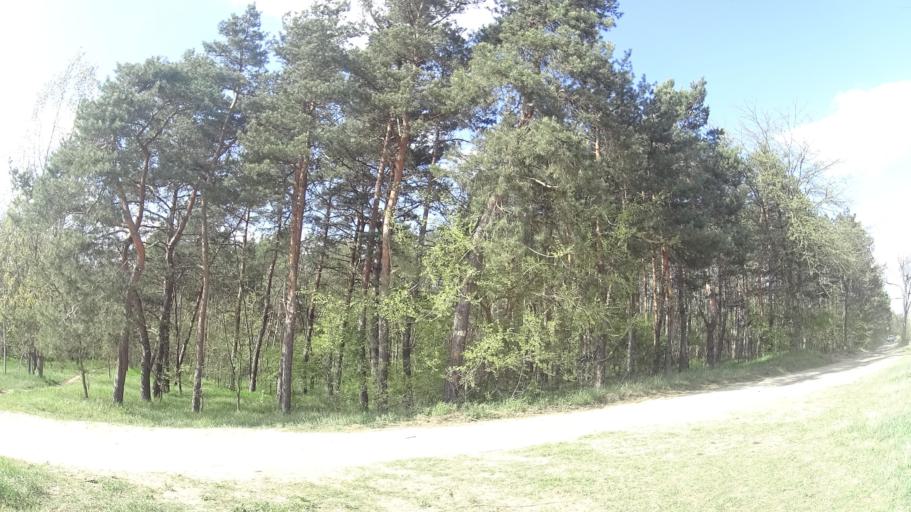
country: HU
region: Pest
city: Veresegyhaz
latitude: 47.6352
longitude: 19.2819
